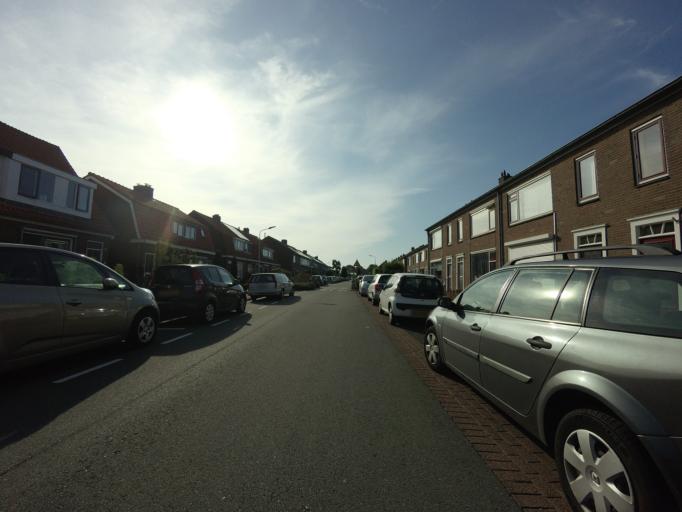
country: NL
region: Utrecht
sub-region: Gemeente Lopik
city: Lopik
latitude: 51.9529
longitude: 4.9640
